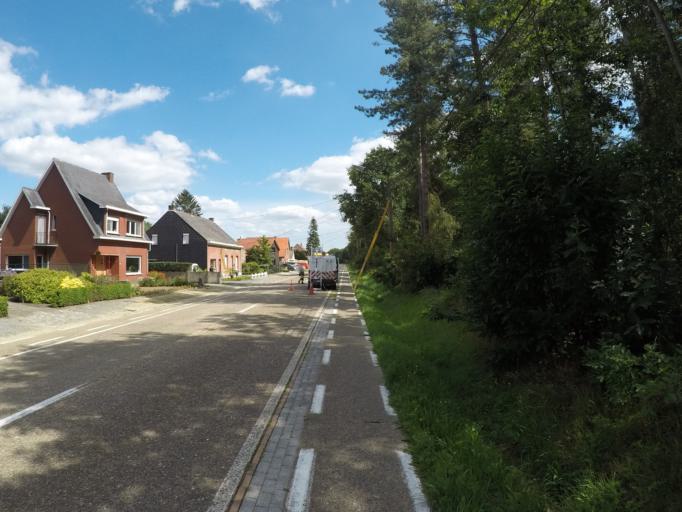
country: BE
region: Flanders
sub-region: Provincie Antwerpen
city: Herenthout
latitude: 51.1432
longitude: 4.7352
